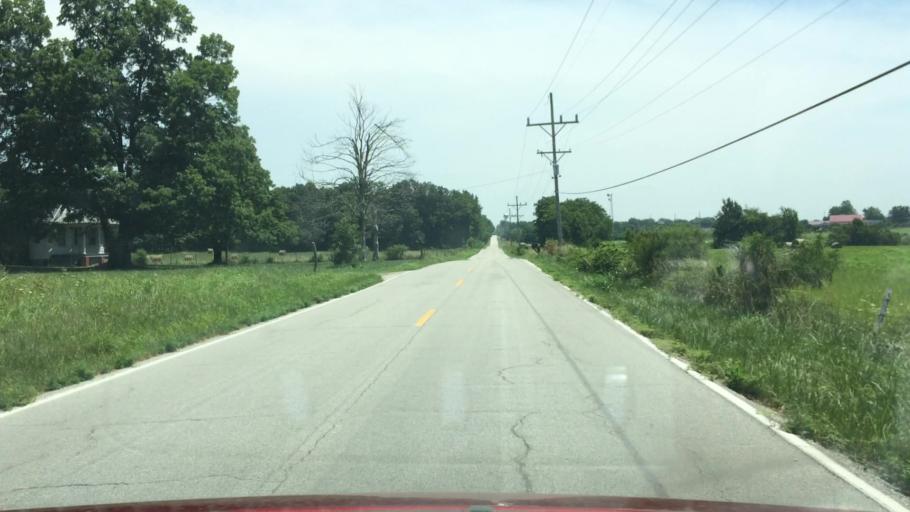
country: US
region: Missouri
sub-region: Greene County
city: Strafford
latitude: 37.2711
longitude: -93.1438
